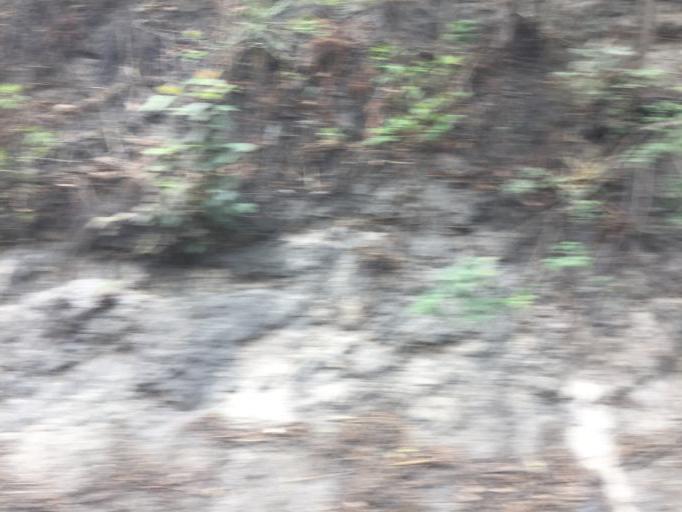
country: GT
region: Guatemala
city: Petapa
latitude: 14.5241
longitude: -90.5553
